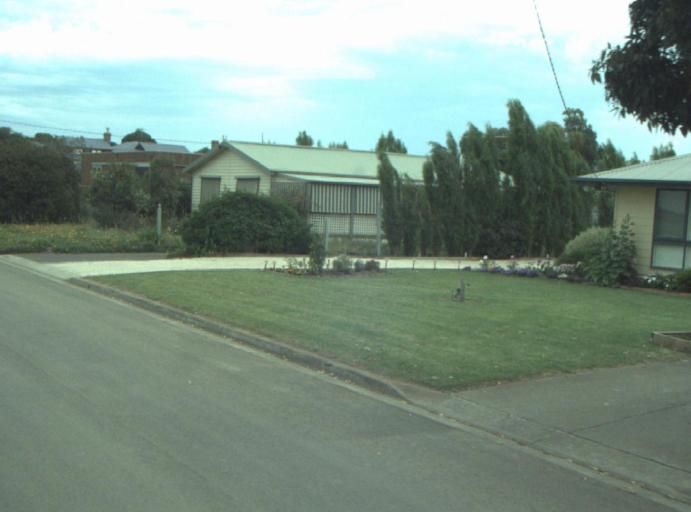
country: AU
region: Victoria
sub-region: Queenscliffe
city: Queenscliff
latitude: -38.1406
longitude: 144.7078
